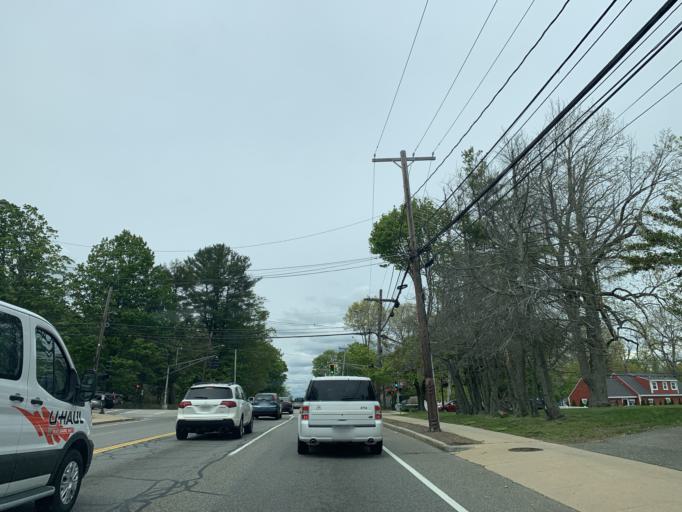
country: US
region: Massachusetts
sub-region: Norfolk County
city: Milton
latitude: 42.2541
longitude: -71.0770
